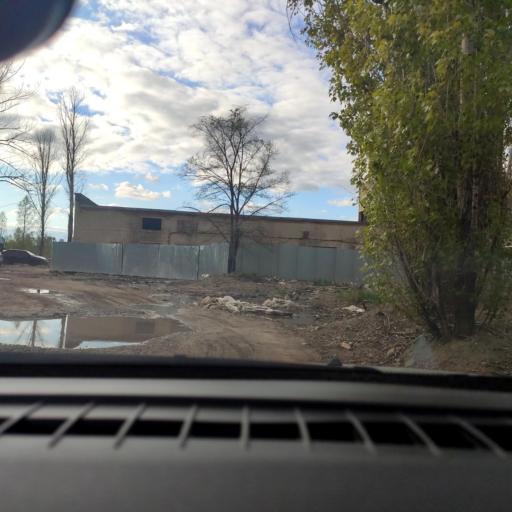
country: RU
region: Voronezj
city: Somovo
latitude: 51.7237
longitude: 39.2856
